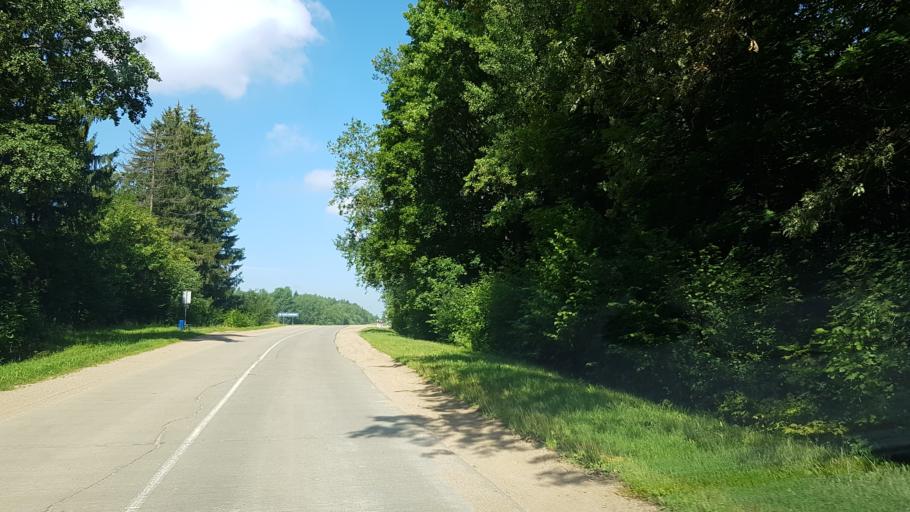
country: BY
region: Minsk
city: Dzyarzhynsk
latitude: 53.7091
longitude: 27.0768
